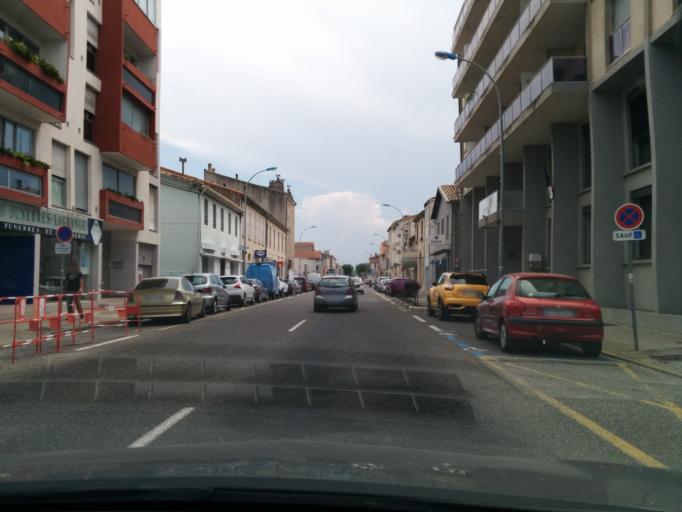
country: FR
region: Languedoc-Roussillon
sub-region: Departement de l'Aude
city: Carcassonne
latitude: 43.2137
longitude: 2.3451
